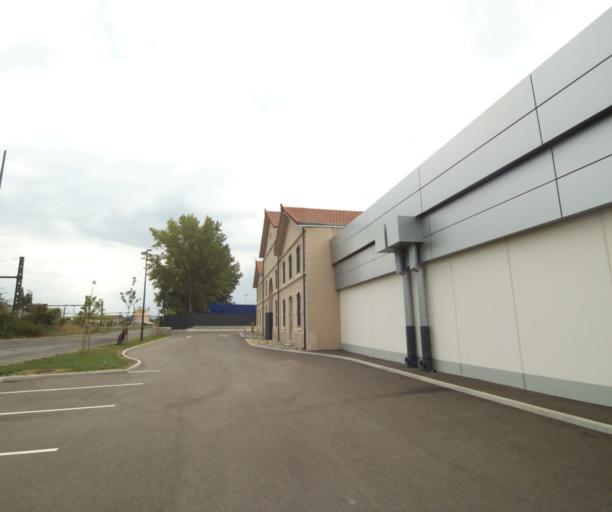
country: FR
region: Bourgogne
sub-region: Departement de Saone-et-Loire
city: Tournus
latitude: 46.5695
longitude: 4.9054
